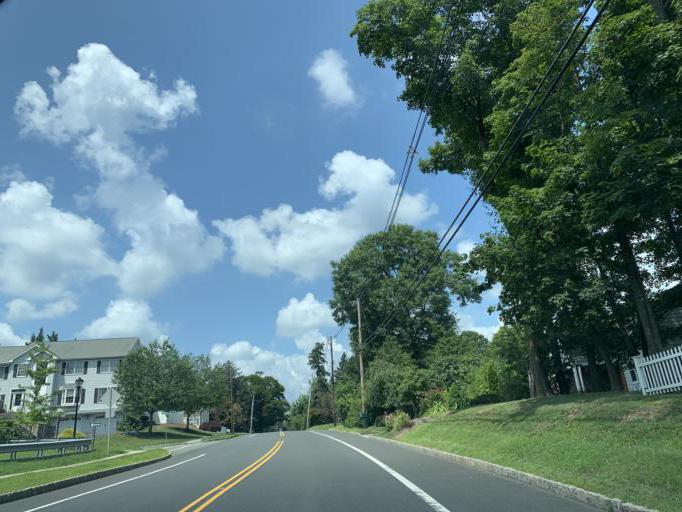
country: US
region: New Jersey
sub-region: Somerset County
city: Bernardsville
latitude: 40.7182
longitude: -74.5566
